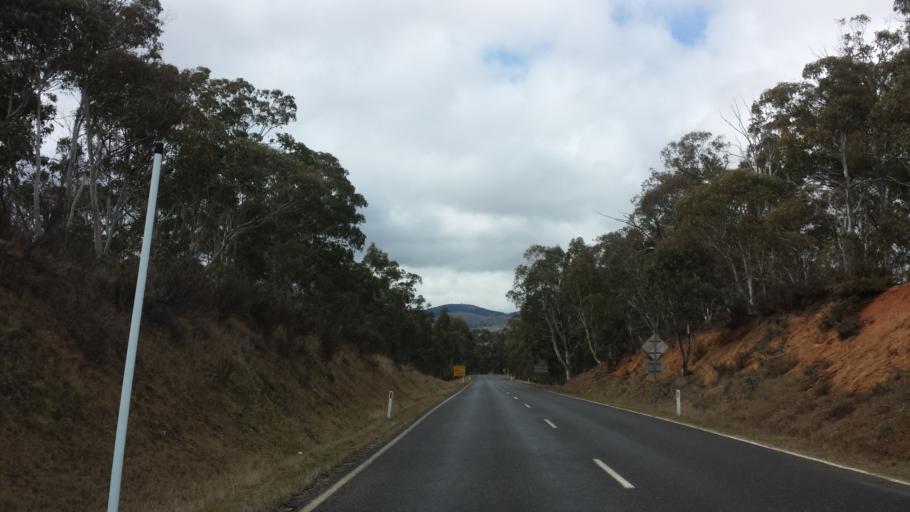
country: AU
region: Victoria
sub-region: Alpine
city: Mount Beauty
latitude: -37.0927
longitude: 147.3825
